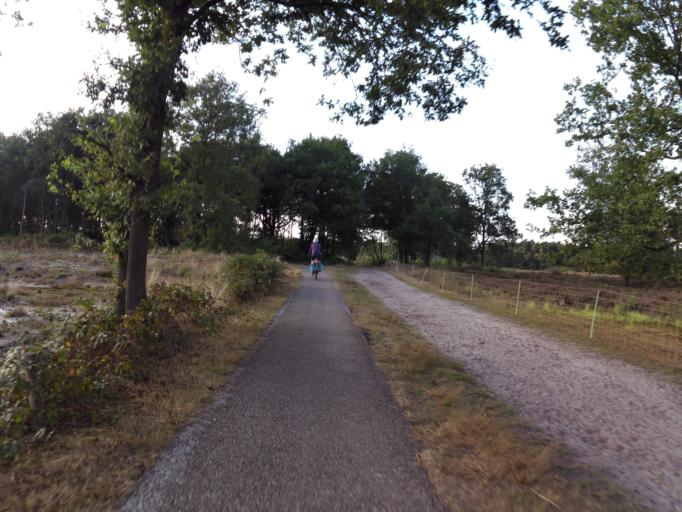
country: NL
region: Gelderland
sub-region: Gemeente Nijmegen
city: Lindenholt
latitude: 51.7851
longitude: 5.8040
